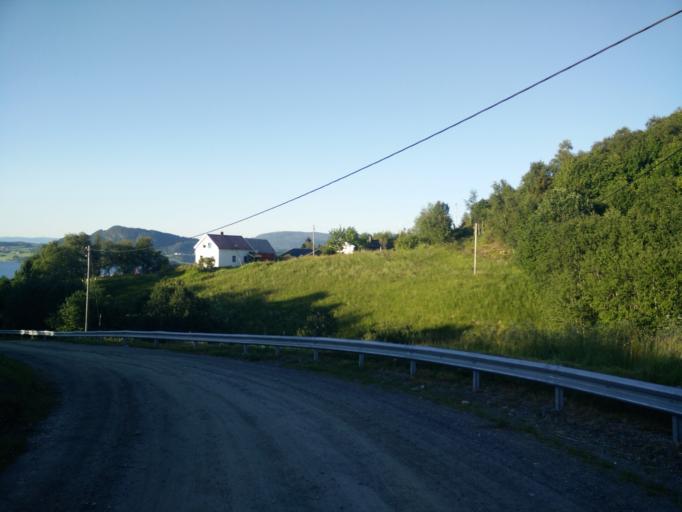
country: NO
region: Sor-Trondelag
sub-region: Skaun
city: Borsa
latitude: 63.3412
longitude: 10.0390
